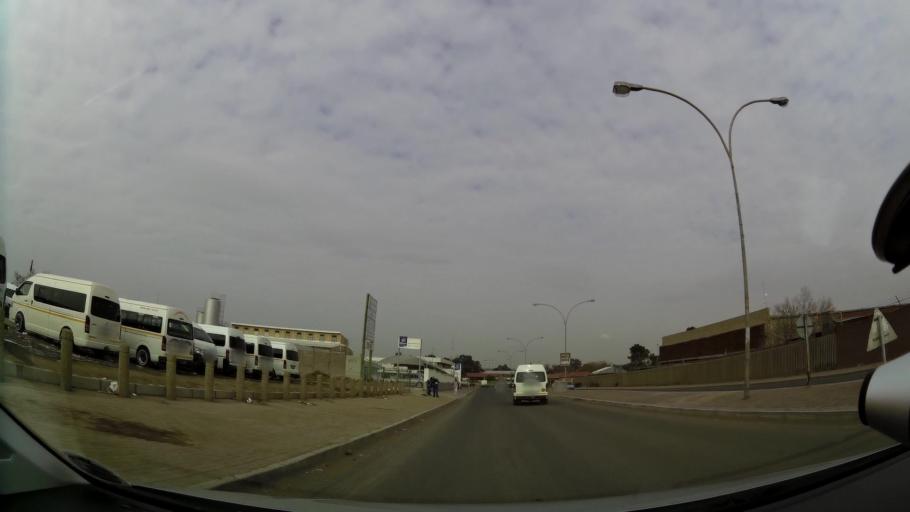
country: ZA
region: Orange Free State
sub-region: Mangaung Metropolitan Municipality
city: Bloemfontein
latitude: -29.1286
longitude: 26.2231
